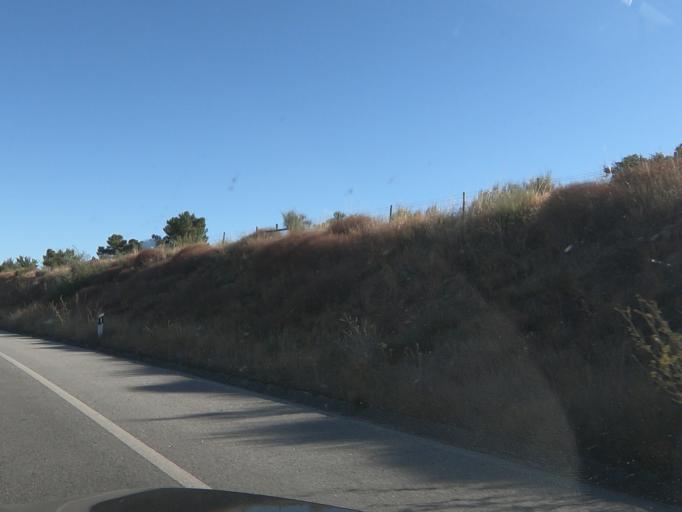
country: PT
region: Vila Real
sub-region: Valpacos
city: Valpacos
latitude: 41.5725
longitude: -7.2993
